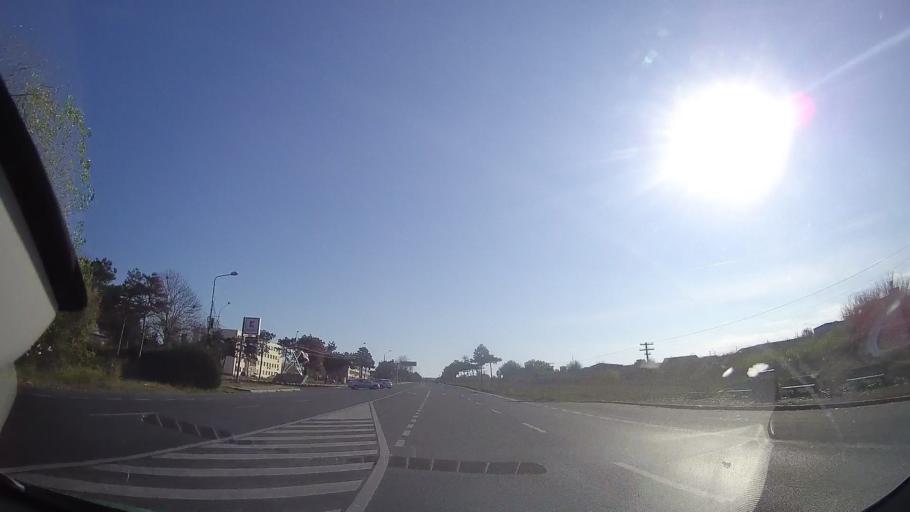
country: RO
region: Constanta
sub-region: Municipiul Mangalia
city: Mangalia
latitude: 43.8298
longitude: 28.5797
